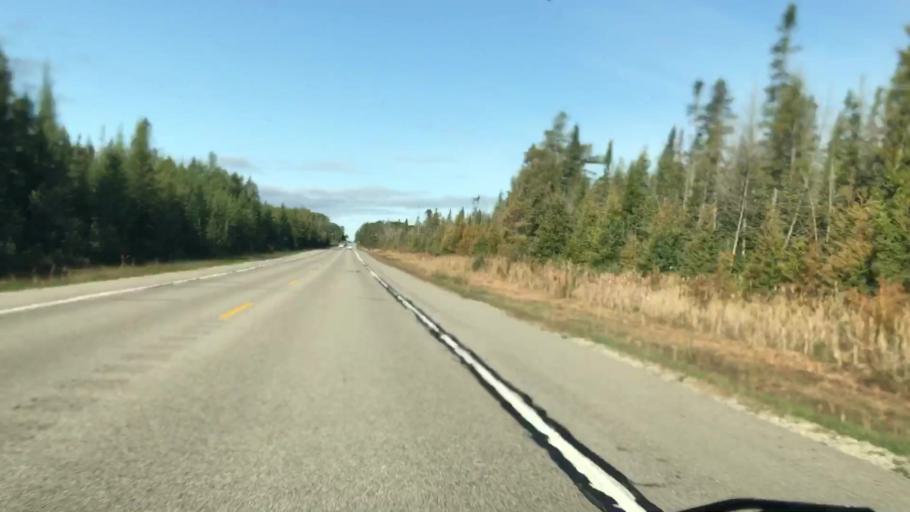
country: US
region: Michigan
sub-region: Luce County
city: Newberry
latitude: 46.3035
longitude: -85.3376
